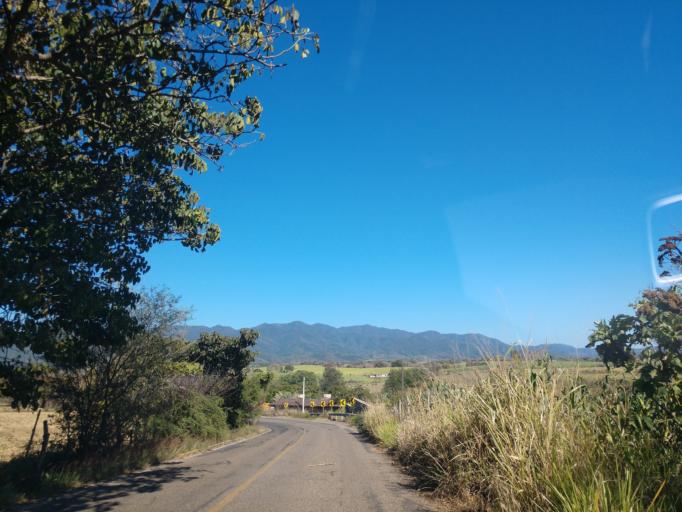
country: MX
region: Nayarit
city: Compostela
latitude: 21.2556
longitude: -104.9008
